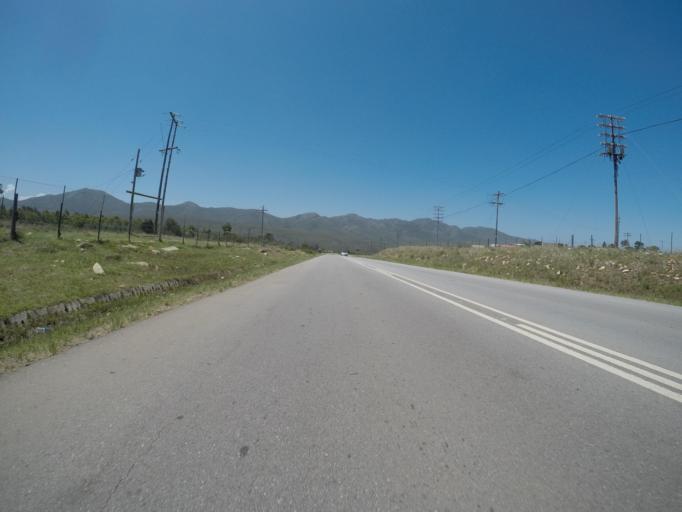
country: ZA
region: Eastern Cape
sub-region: Cacadu District Municipality
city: Kareedouw
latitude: -33.9513
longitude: 24.3007
